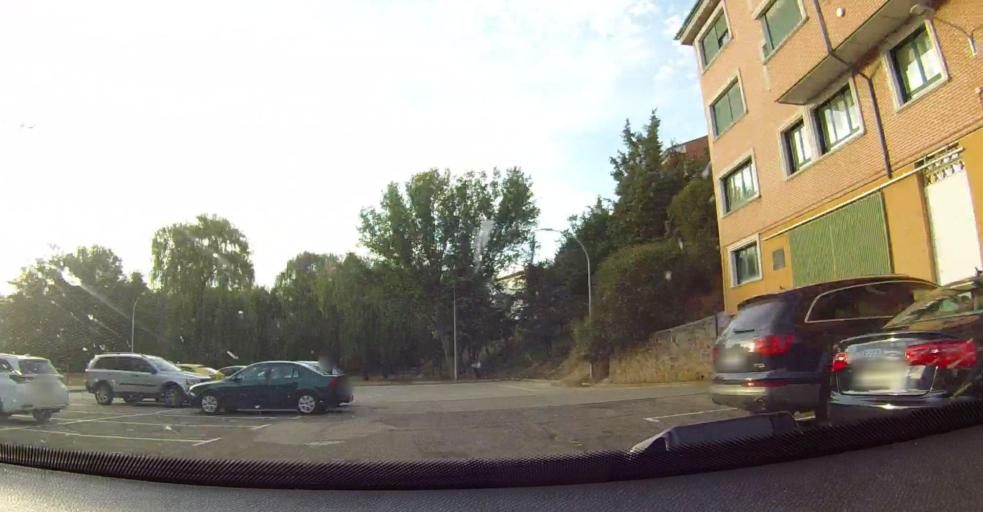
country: ES
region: Castille and Leon
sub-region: Provincia de Palencia
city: Carrion de los Condes
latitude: 42.3378
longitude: -4.6056
